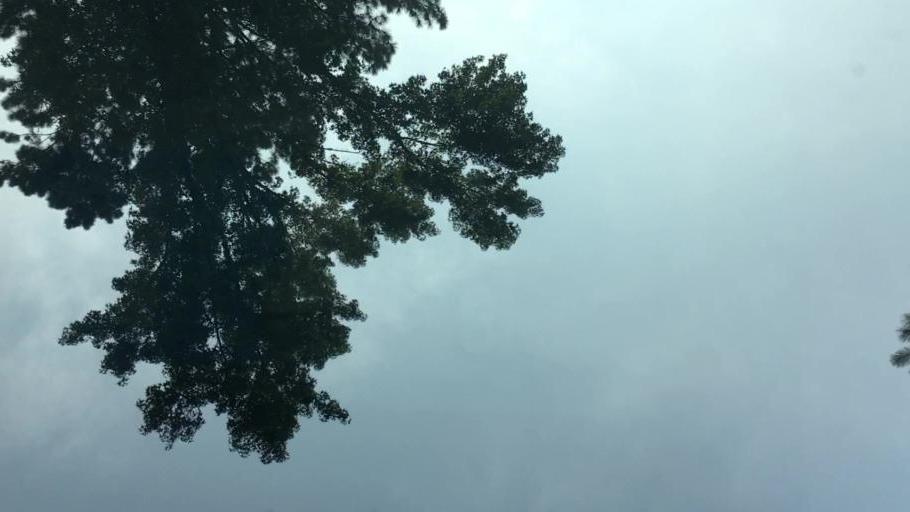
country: US
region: Alabama
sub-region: Bibb County
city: Woodstock
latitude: 33.2162
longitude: -87.0733
